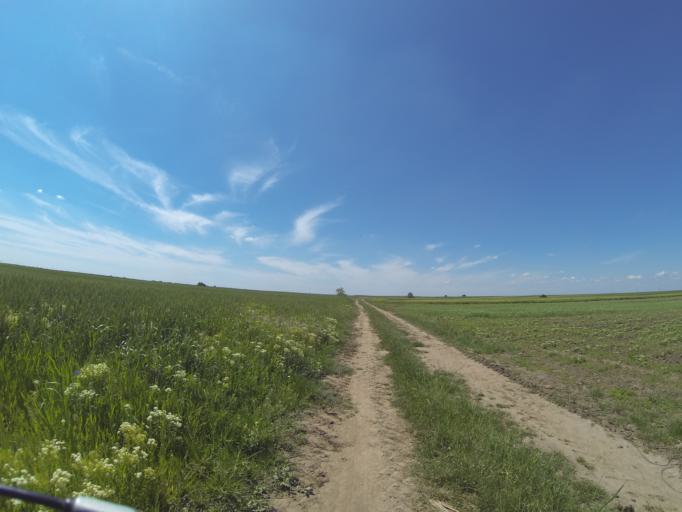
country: RO
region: Dolj
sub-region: Comuna Leu
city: Leu
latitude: 44.2135
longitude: 24.0267
